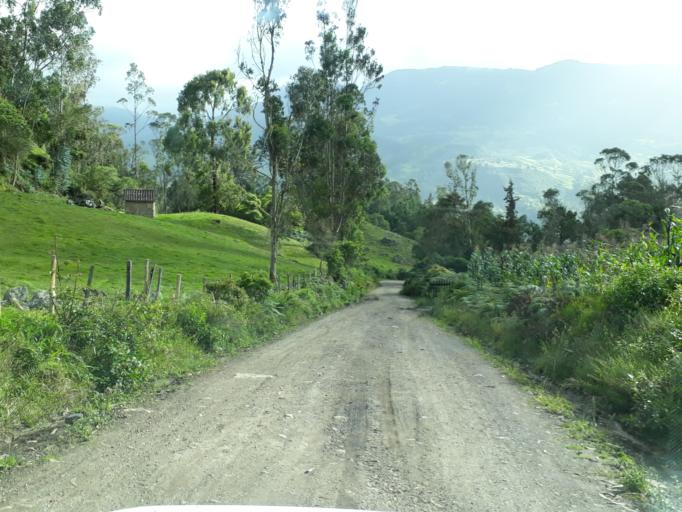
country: CO
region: Cundinamarca
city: Junin
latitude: 4.7835
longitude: -73.6841
